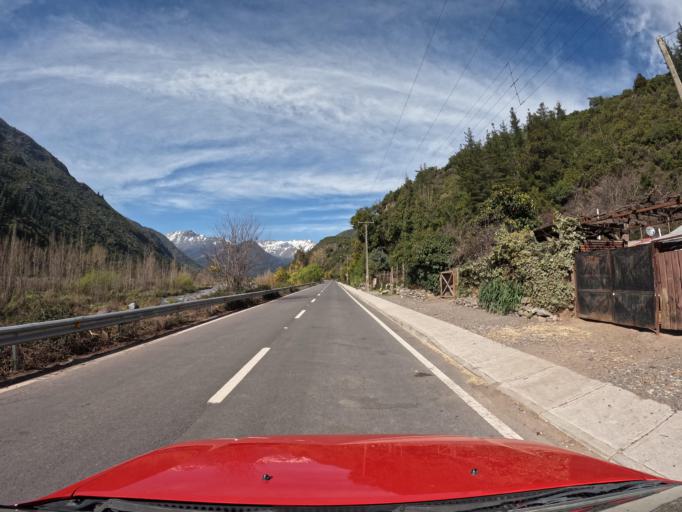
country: CL
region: O'Higgins
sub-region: Provincia de Colchagua
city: Chimbarongo
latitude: -35.0001
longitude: -70.8069
